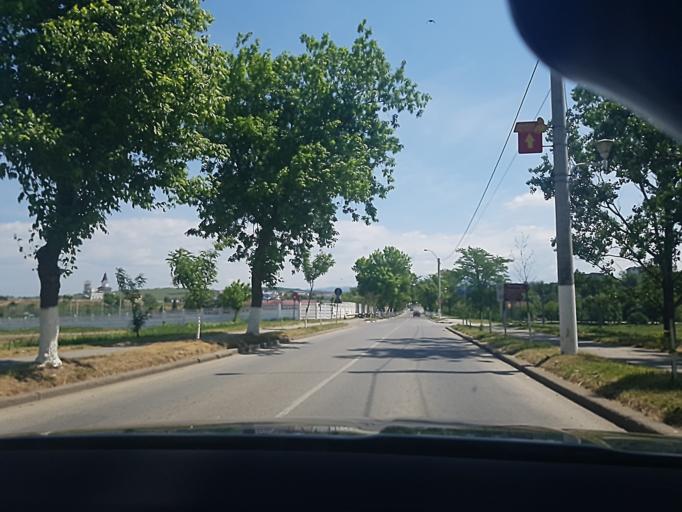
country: RO
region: Hunedoara
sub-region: Comuna Calan
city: Calan
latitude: 45.7340
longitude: 23.0172
